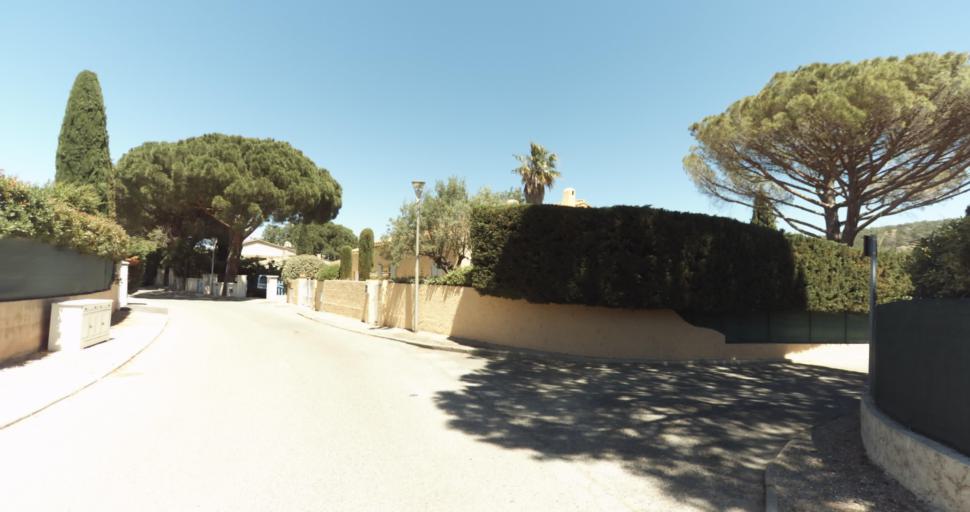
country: FR
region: Provence-Alpes-Cote d'Azur
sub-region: Departement du Var
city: Gassin
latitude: 43.2450
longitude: 6.5684
